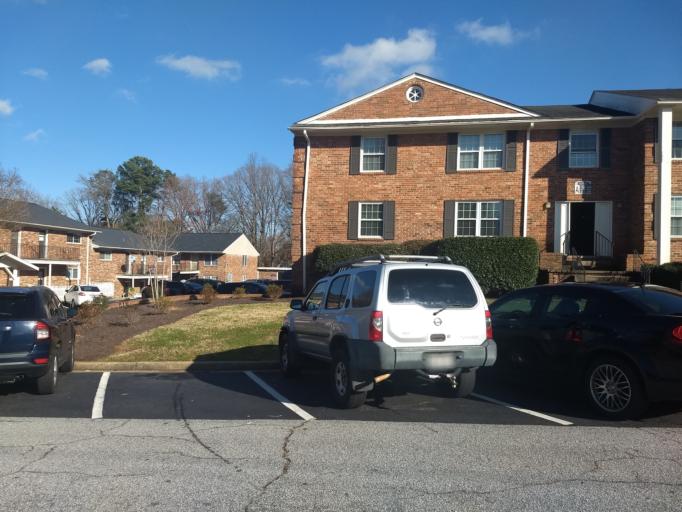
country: US
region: South Carolina
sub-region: Greenville County
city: Wade Hampton
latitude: 34.8701
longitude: -82.3518
